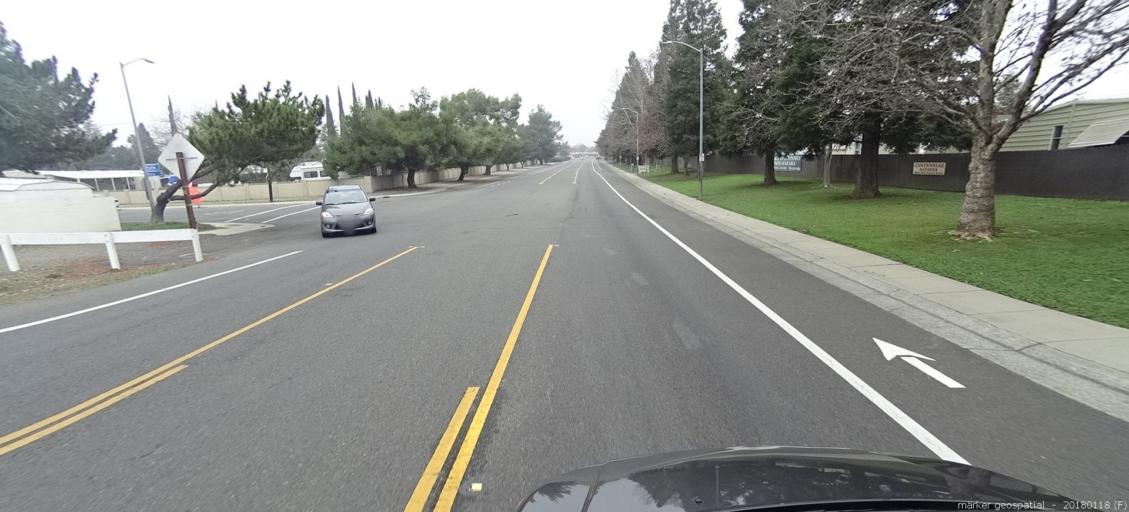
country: US
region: California
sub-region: Sacramento County
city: Rancho Cordova
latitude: 38.5768
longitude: -121.3183
